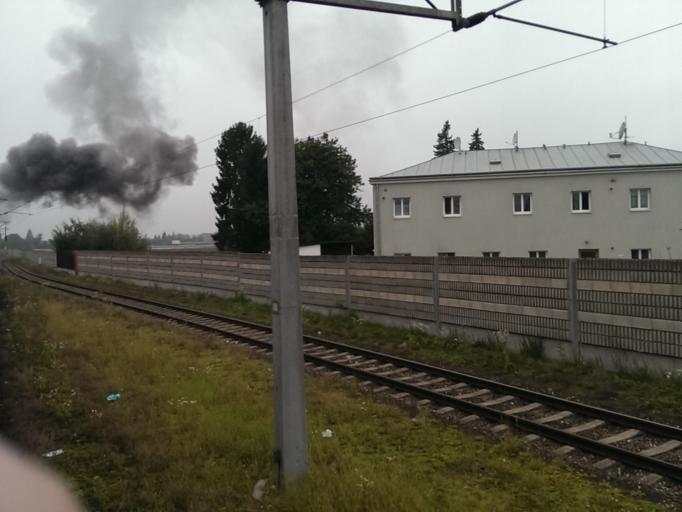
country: AT
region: Upper Austria
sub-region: Politischer Bezirk Linz-Land
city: Horsching
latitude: 48.2448
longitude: 14.1842
